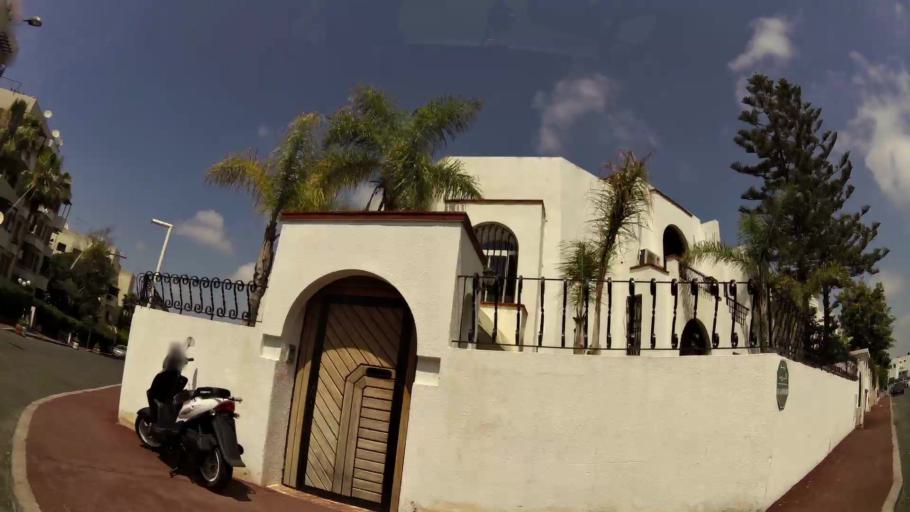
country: MA
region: Rabat-Sale-Zemmour-Zaer
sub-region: Skhirate-Temara
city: Temara
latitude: 33.9625
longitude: -6.8758
